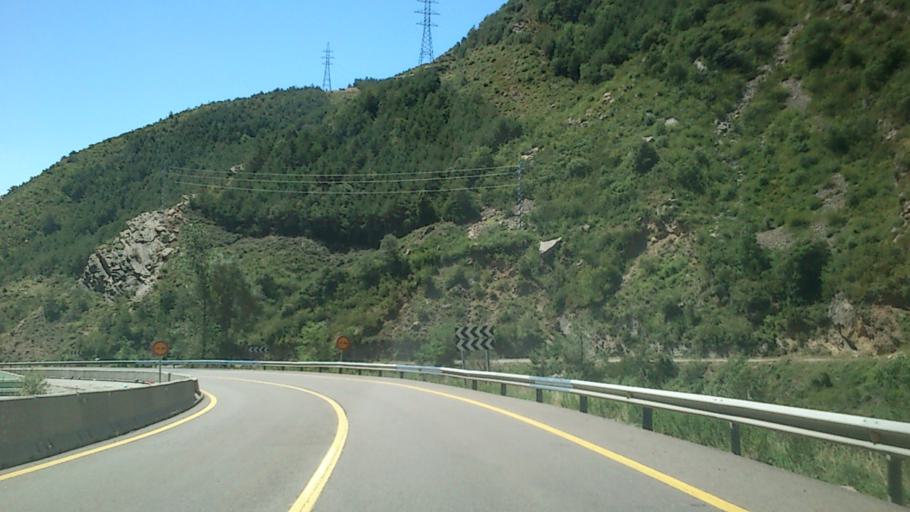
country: ES
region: Aragon
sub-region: Provincia de Huesca
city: Arguis
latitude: 42.2981
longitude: -0.4267
